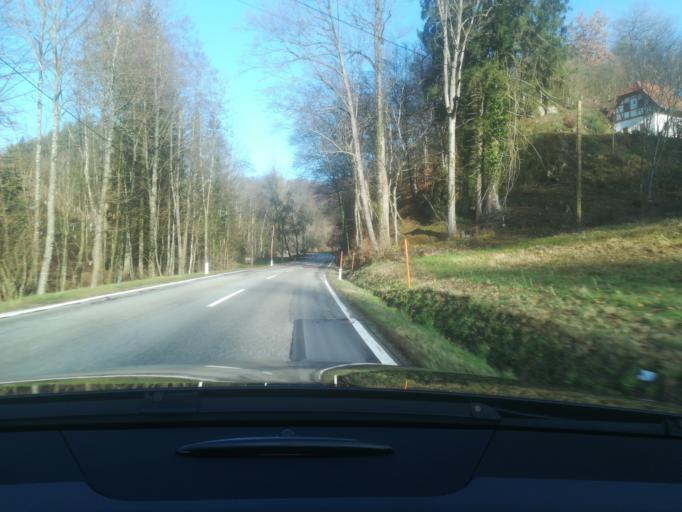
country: AT
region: Upper Austria
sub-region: Politischer Bezirk Urfahr-Umgebung
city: Feldkirchen an der Donau
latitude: 48.3760
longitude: 14.0632
